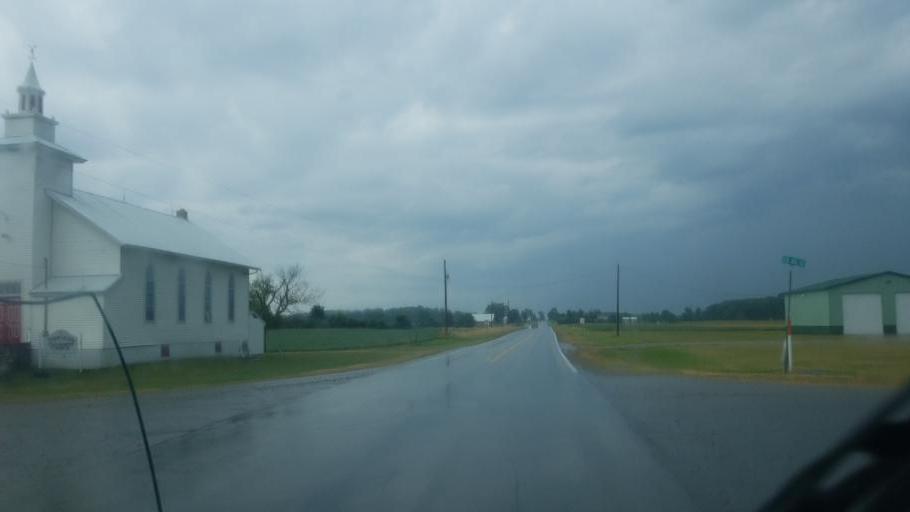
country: US
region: Indiana
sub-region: DeKalb County
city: Butler
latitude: 41.4871
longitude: -84.8726
